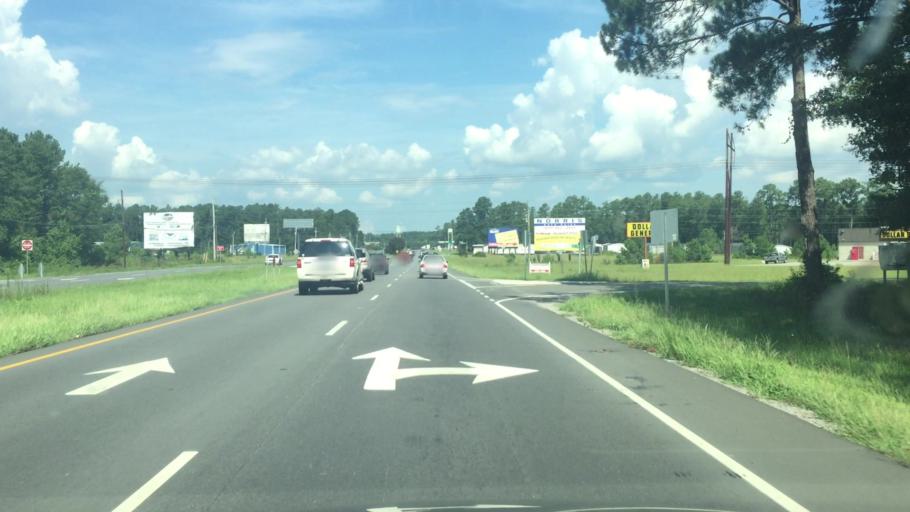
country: US
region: North Carolina
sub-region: Scotland County
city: Laurel Hill
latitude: 34.8019
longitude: -79.5371
